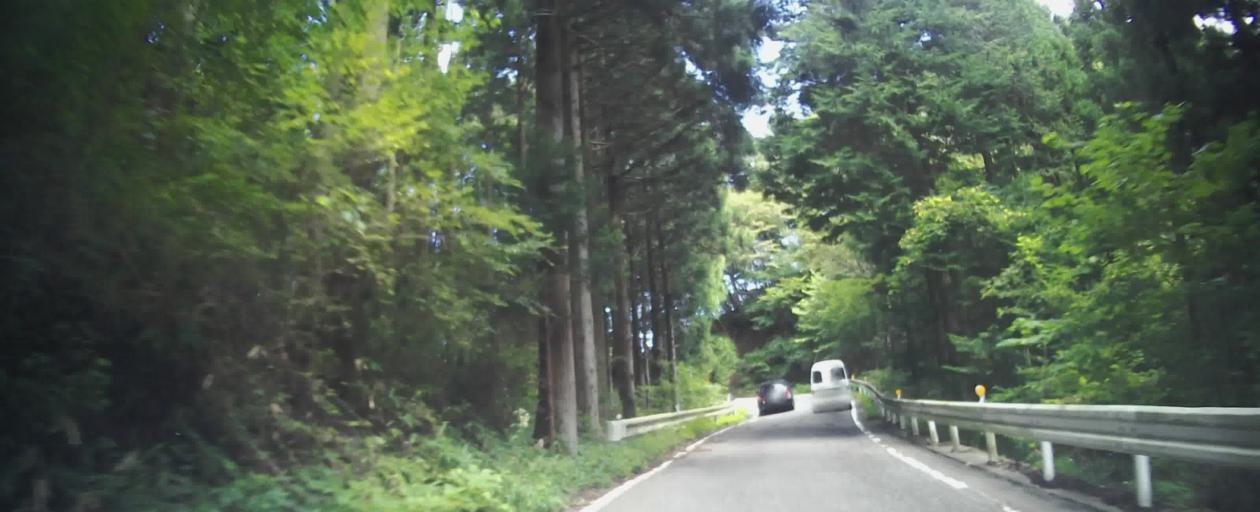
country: JP
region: Gunma
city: Shibukawa
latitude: 36.4585
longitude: 138.8975
